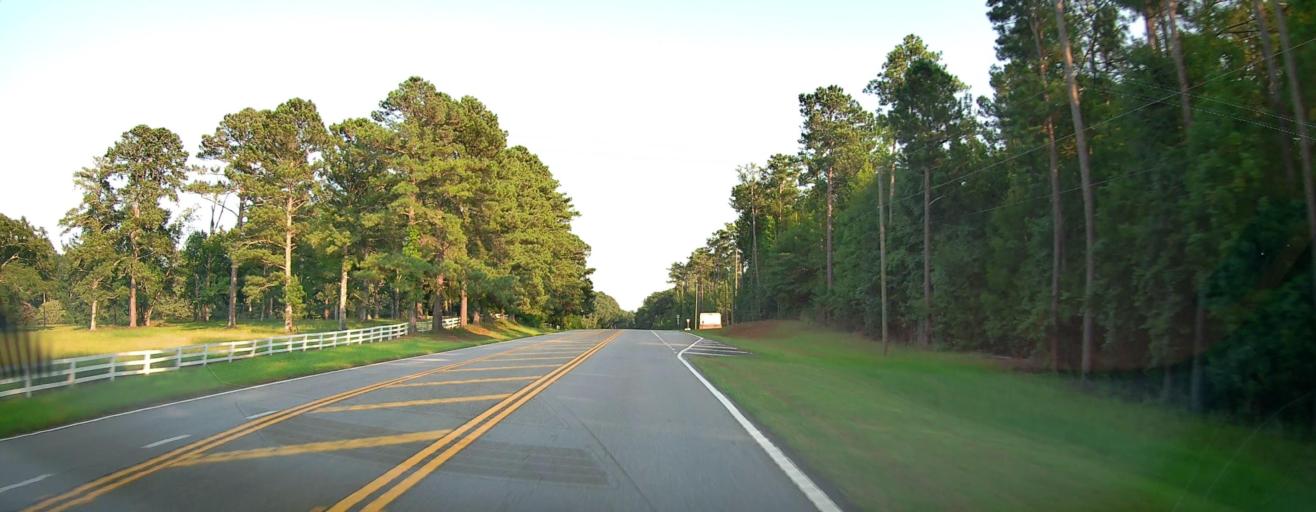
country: US
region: Georgia
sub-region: Bibb County
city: West Point
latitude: 32.9028
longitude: -83.7692
